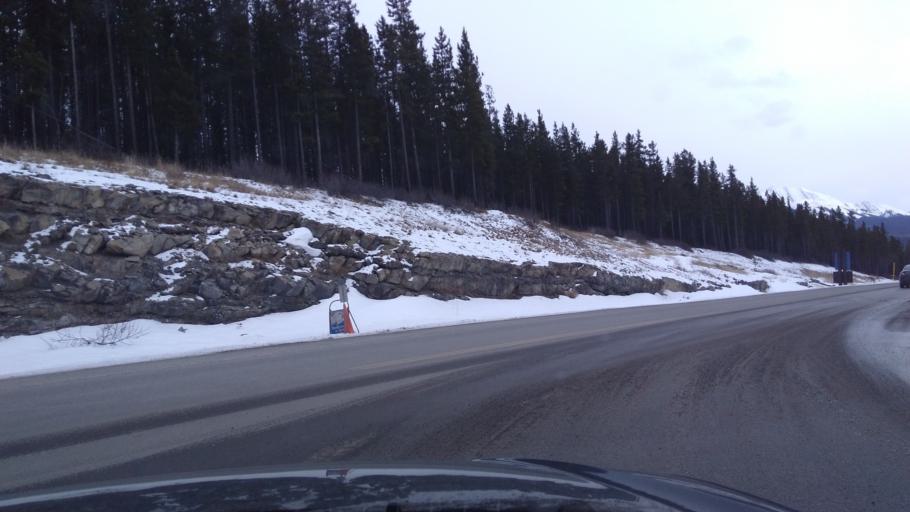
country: CA
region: Alberta
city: Canmore
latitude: 50.9398
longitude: -115.1498
